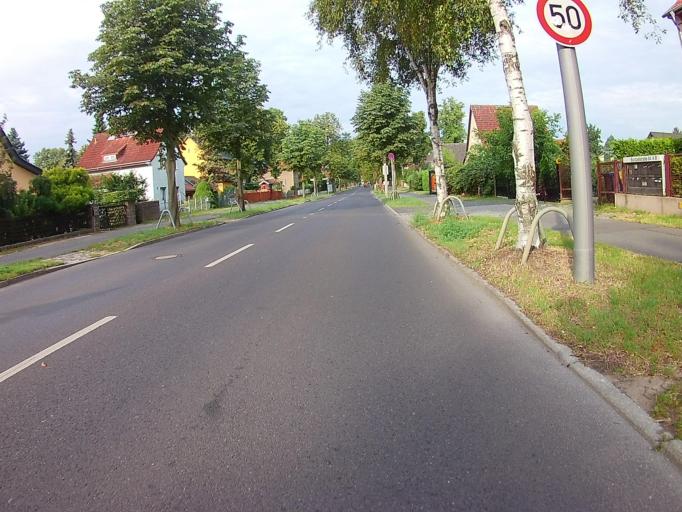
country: DE
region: Berlin
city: Bohnsdorf
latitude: 52.4034
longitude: 13.5692
